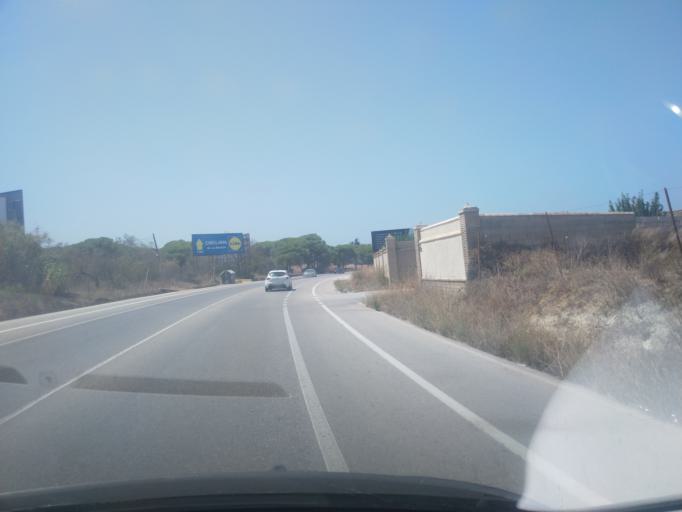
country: ES
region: Andalusia
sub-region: Provincia de Cadiz
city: Chiclana de la Frontera
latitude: 36.3887
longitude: -6.1379
